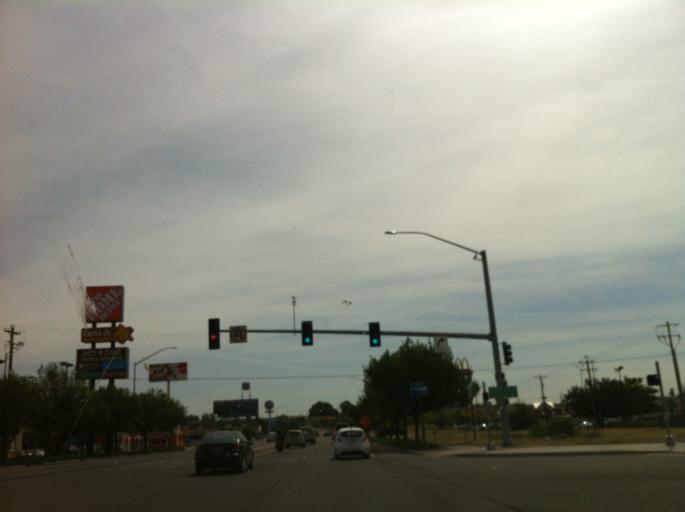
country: US
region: Oregon
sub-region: Malheur County
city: Ontario
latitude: 44.0247
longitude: -116.9460
